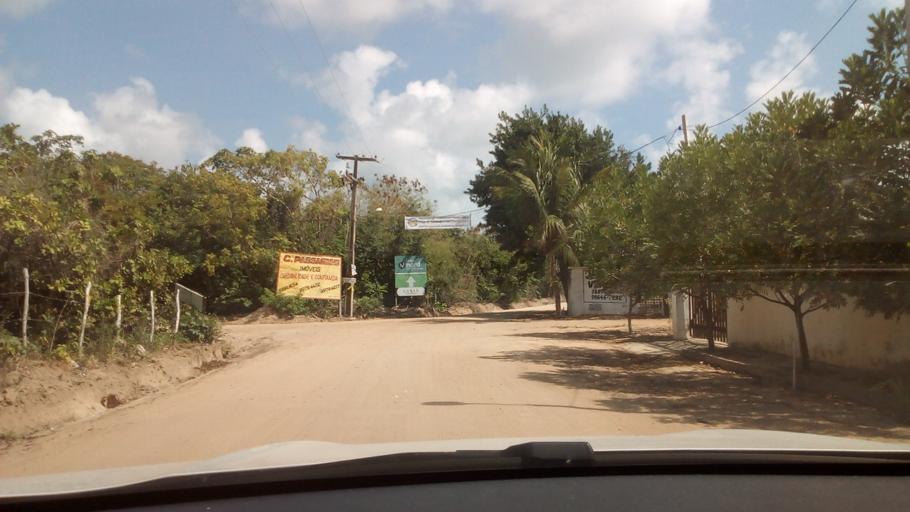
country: BR
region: Paraiba
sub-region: Conde
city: Conde
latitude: -7.3164
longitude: -34.8049
